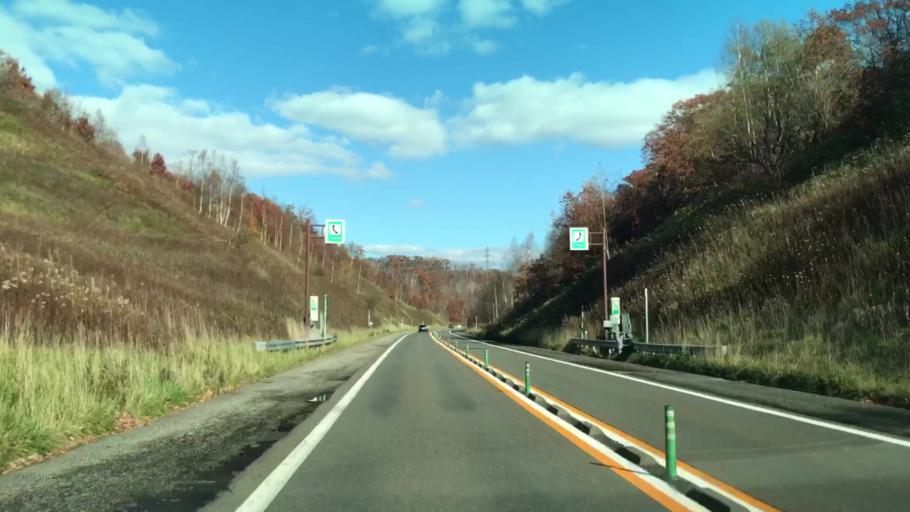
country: JP
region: Hokkaido
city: Chitose
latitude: 42.8838
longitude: 141.7597
